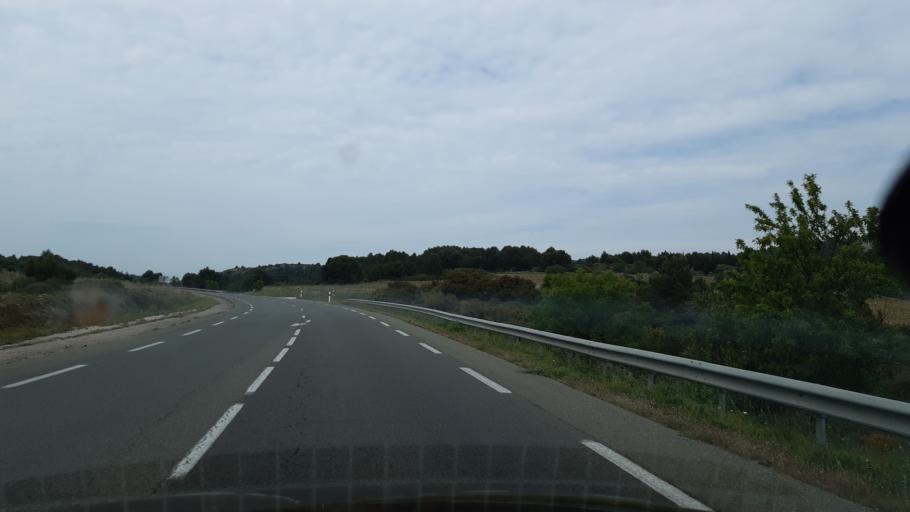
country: FR
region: Languedoc-Roussillon
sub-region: Departement de l'Aude
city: Gruissan
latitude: 43.1226
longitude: 3.0744
